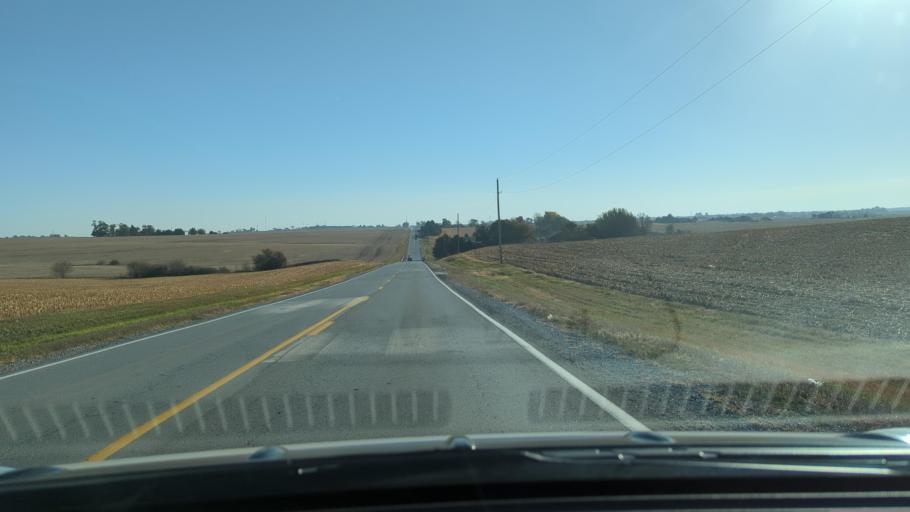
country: US
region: Nebraska
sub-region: Sarpy County
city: Springfield
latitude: 41.0891
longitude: -96.1131
